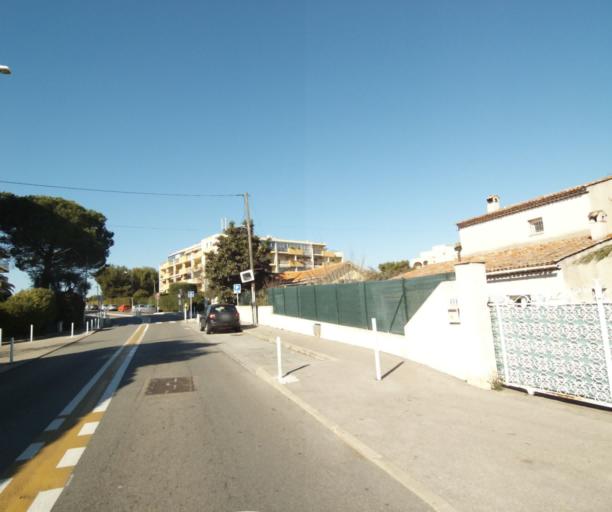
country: FR
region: Provence-Alpes-Cote d'Azur
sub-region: Departement des Alpes-Maritimes
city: Biot
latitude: 43.5969
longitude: 7.0979
